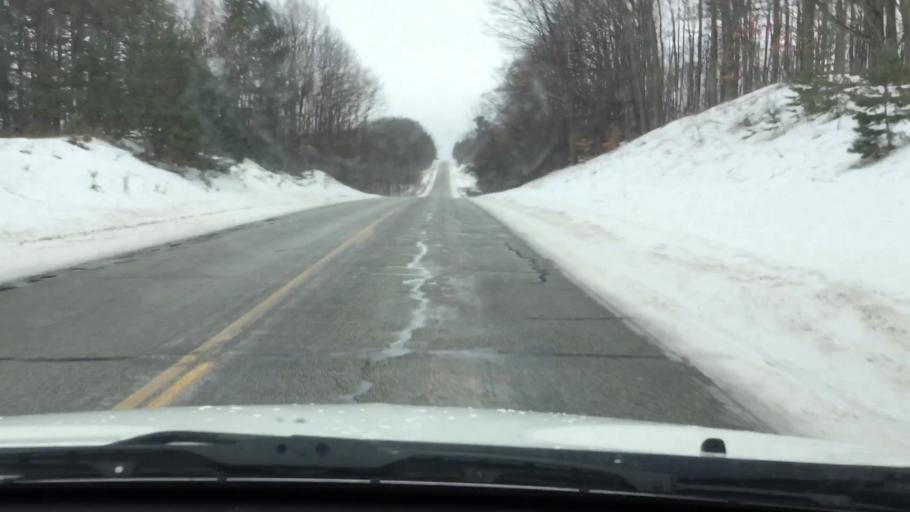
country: US
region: Michigan
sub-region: Wexford County
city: Cadillac
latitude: 44.1740
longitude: -85.4055
